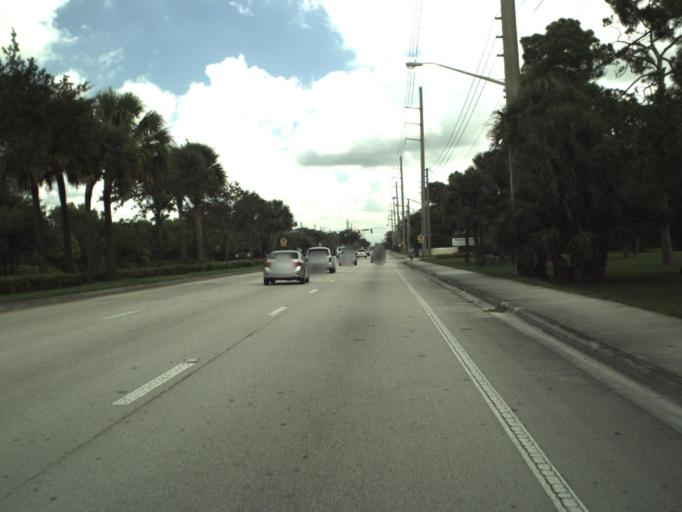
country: US
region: Florida
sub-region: Palm Beach County
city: Royal Palm Estates
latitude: 26.6568
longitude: -80.1452
